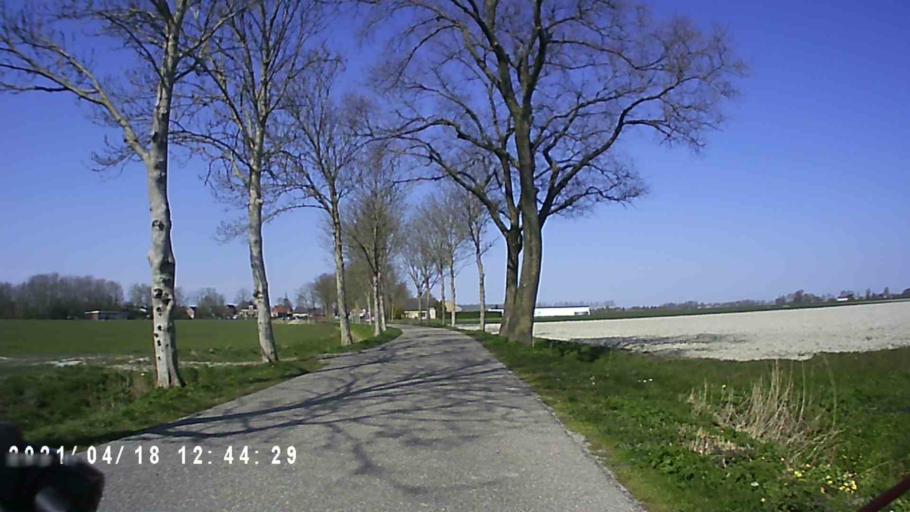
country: NL
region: Friesland
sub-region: Gemeente Dantumadiel
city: Walterswald
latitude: 53.3632
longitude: 6.0555
